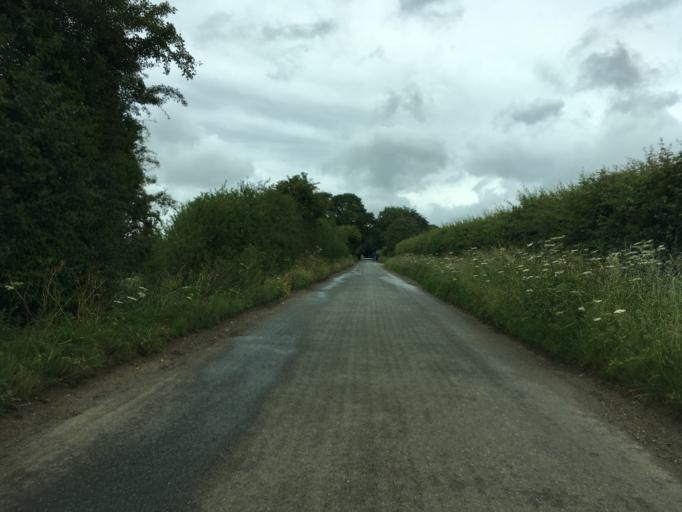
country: GB
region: England
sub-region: Gloucestershire
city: Mickleton
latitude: 52.0735
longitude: -1.7343
